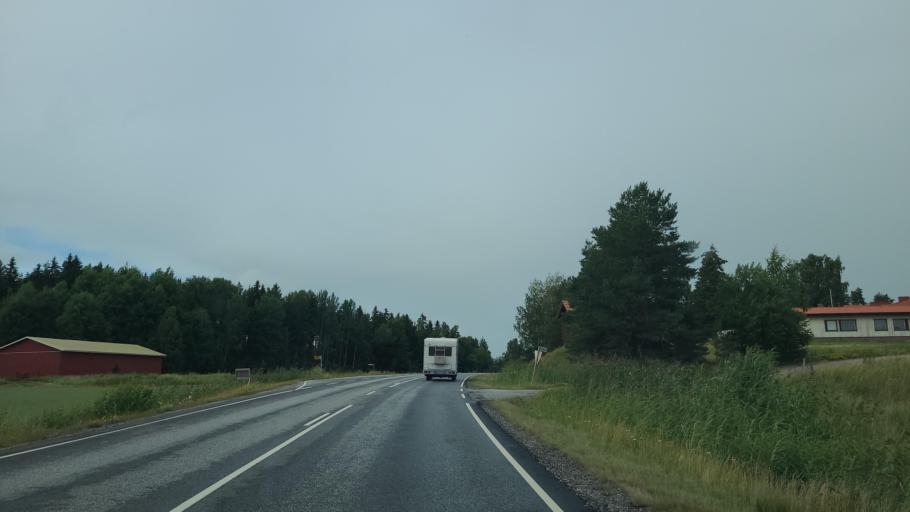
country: FI
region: Varsinais-Suomi
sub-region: Turku
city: Sauvo
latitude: 60.2900
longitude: 22.6726
